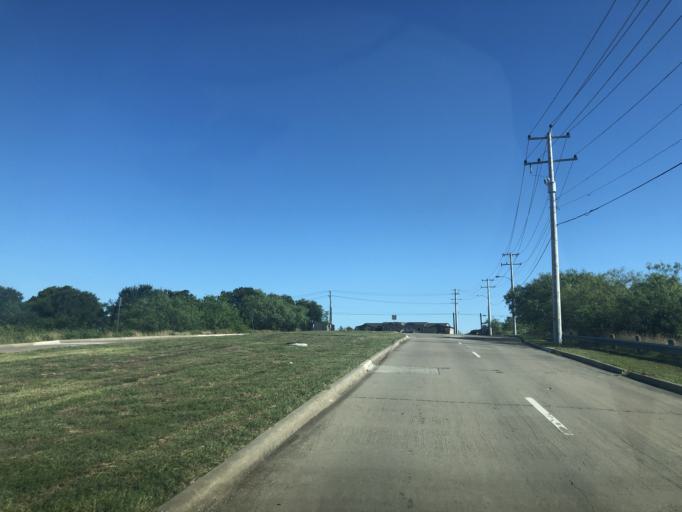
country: US
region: Texas
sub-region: Dallas County
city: Duncanville
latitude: 32.6607
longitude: -96.9639
